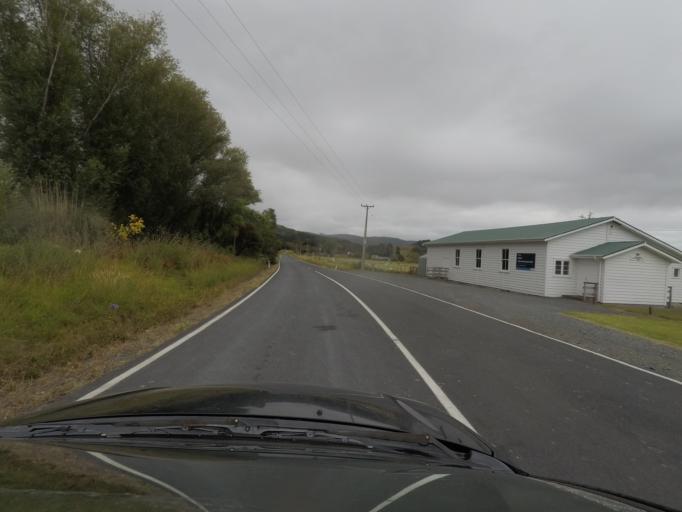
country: NZ
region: Auckland
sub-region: Auckland
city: Warkworth
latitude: -36.2643
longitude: 174.7271
